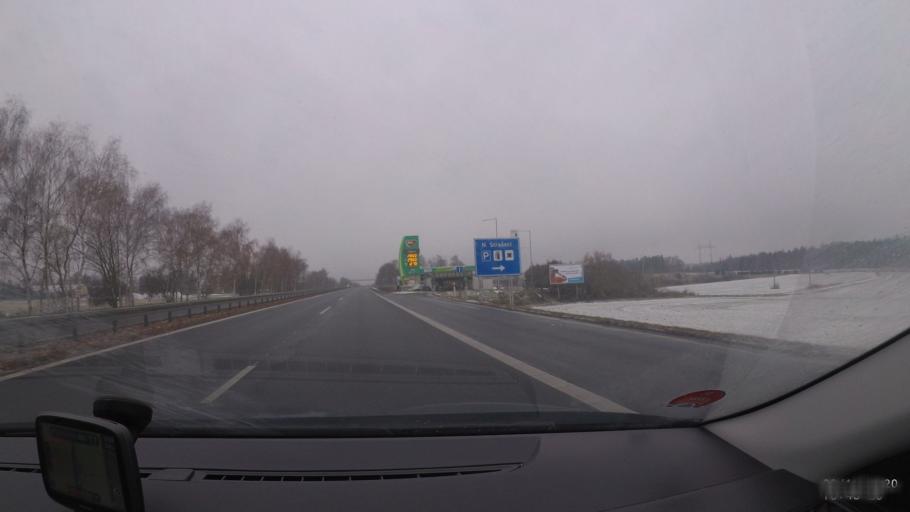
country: CZ
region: Central Bohemia
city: Nove Straseci
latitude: 50.1607
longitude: 13.9073
